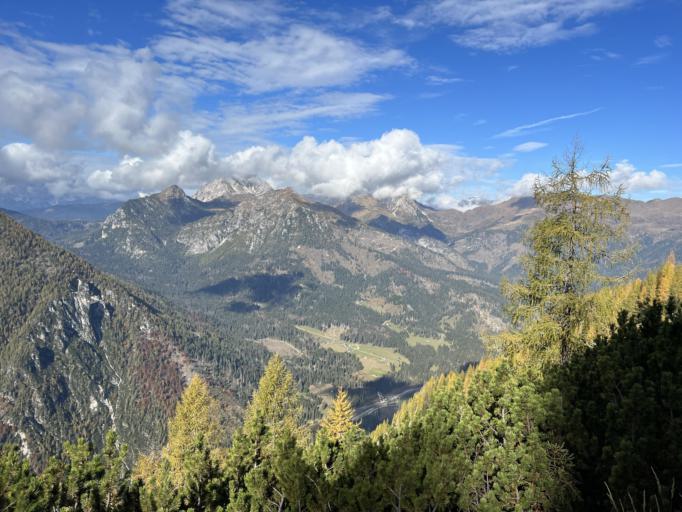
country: IT
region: Veneto
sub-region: Provincia di Belluno
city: Sappada
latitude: 46.5942
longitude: 12.6471
